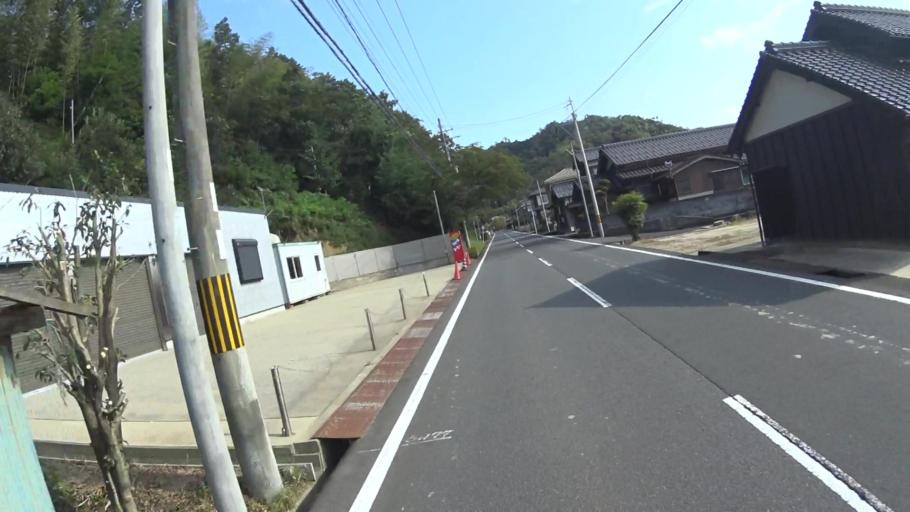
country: JP
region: Kyoto
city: Miyazu
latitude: 35.5777
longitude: 135.1009
